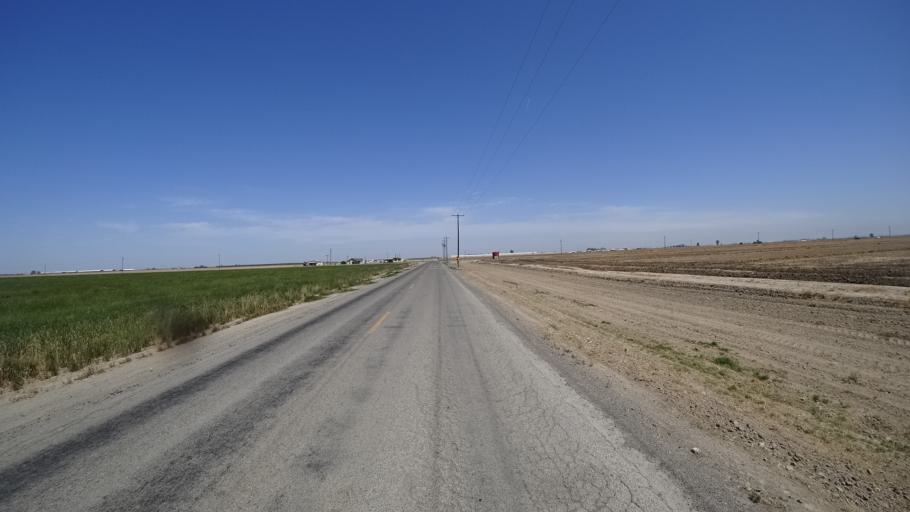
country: US
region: California
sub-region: Kings County
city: Armona
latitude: 36.2090
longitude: -119.6907
